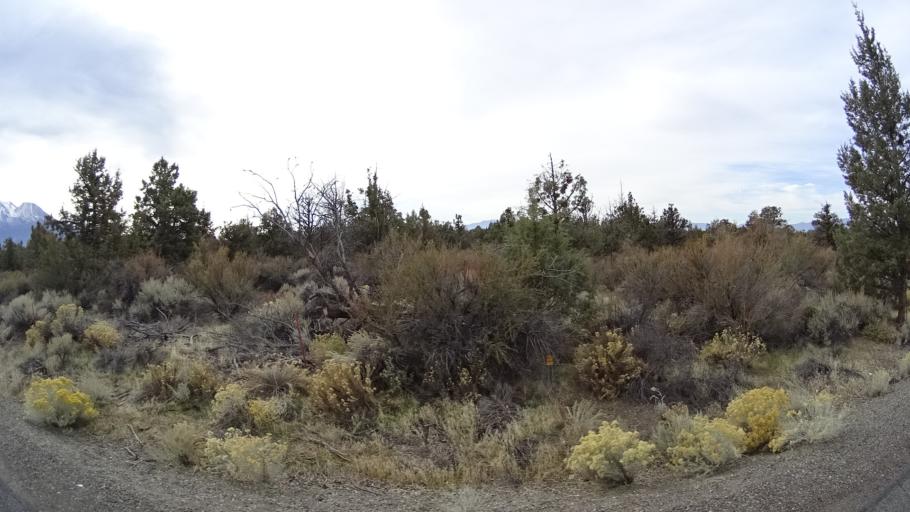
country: US
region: California
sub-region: Siskiyou County
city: Weed
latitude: 41.5828
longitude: -122.2926
